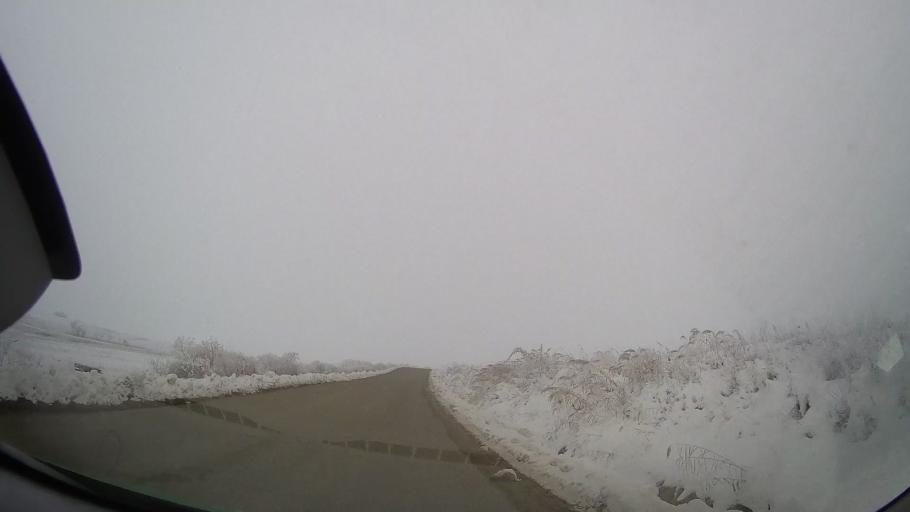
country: RO
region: Iasi
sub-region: Comuna Tansa
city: Suhulet
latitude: 46.8852
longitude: 27.2759
